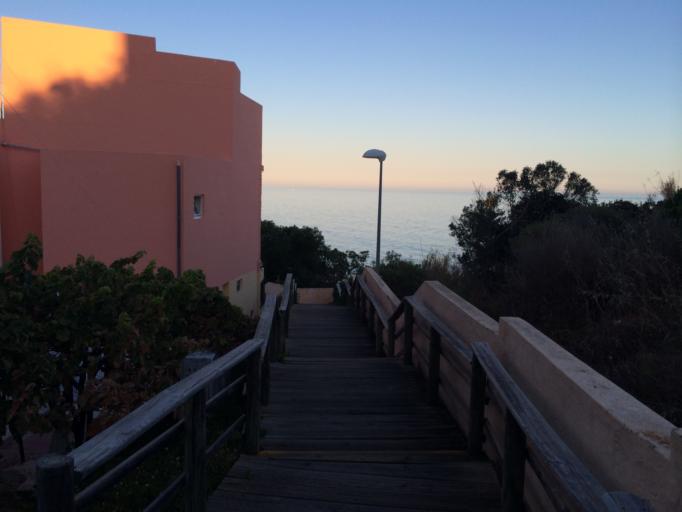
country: PT
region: Faro
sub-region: Loule
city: Boliqueime
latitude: 37.0902
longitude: -8.1913
